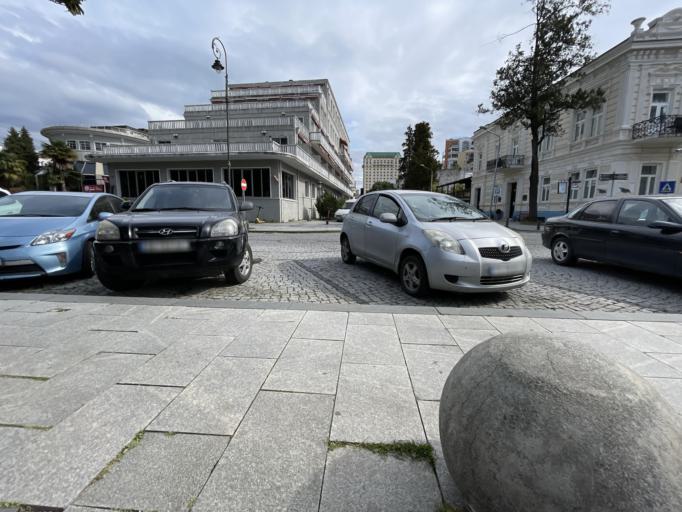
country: GE
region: Ajaria
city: Batumi
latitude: 41.6529
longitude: 41.6343
